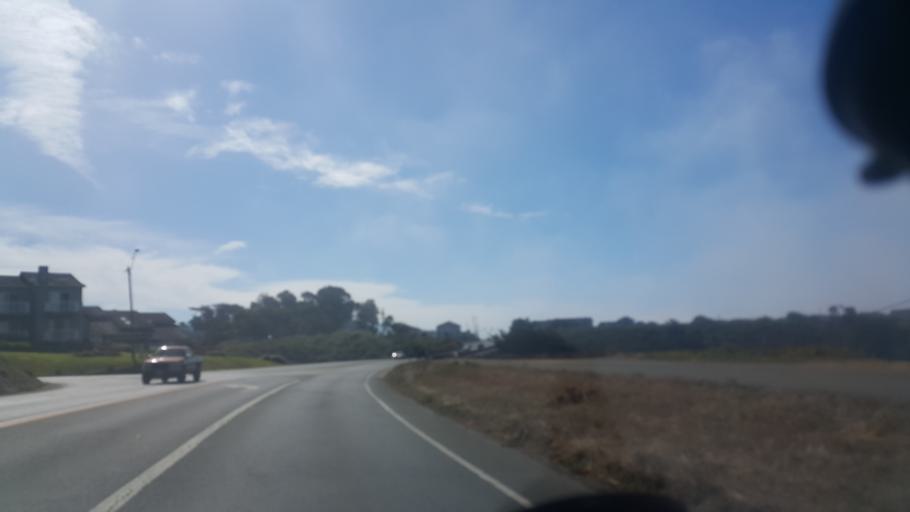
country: US
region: California
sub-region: Mendocino County
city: Fort Bragg
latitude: 39.4561
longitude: -123.8057
